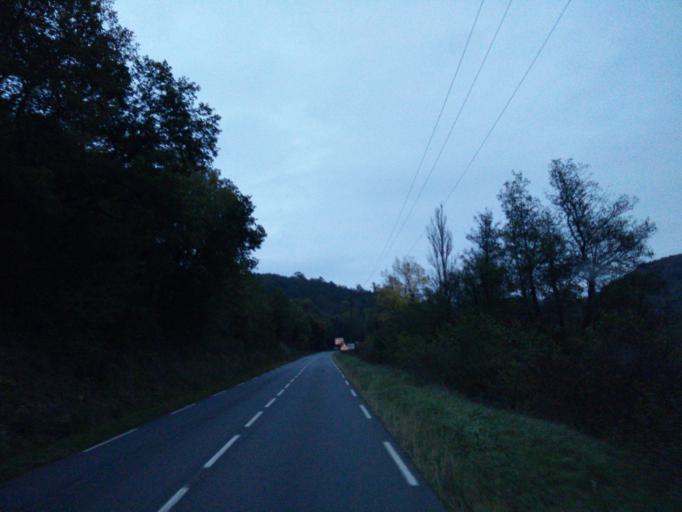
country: FR
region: Aquitaine
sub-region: Departement de la Dordogne
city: Saint-Cyprien
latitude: 44.9275
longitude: 1.0777
